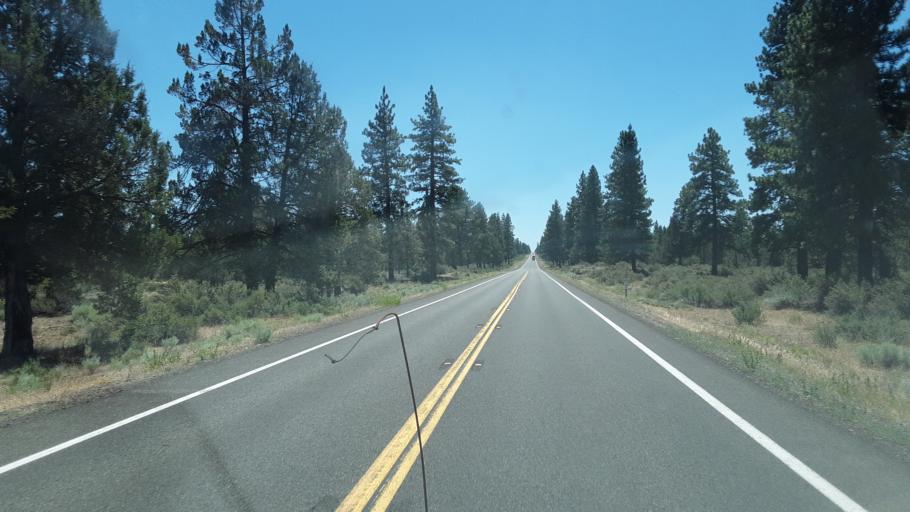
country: US
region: California
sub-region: Siskiyou County
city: Tulelake
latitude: 41.6285
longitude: -121.2254
